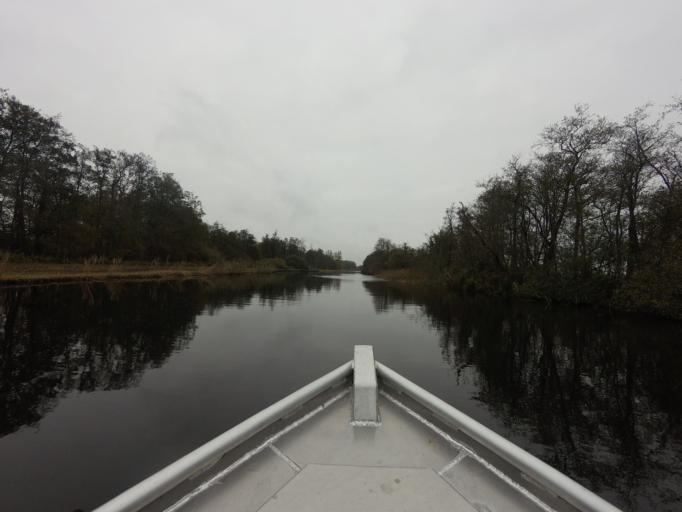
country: NL
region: Overijssel
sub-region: Gemeente Steenwijkerland
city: Oldemarkt
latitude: 52.7768
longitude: 5.9735
